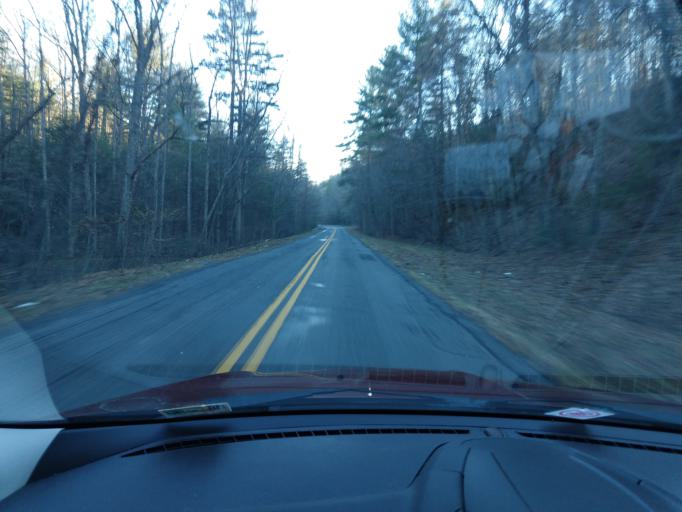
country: US
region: Virginia
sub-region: Alleghany County
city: Clifton Forge
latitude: 37.8359
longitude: -79.8453
